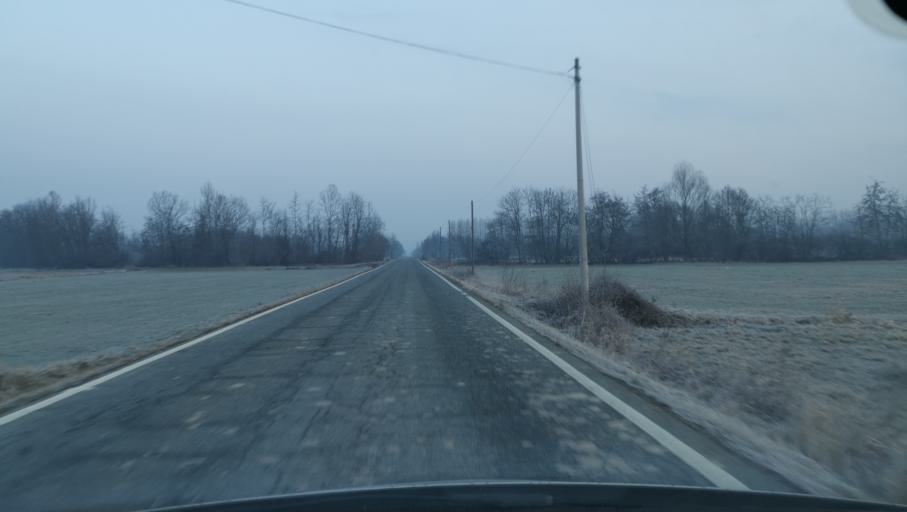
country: IT
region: Piedmont
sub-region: Provincia di Torino
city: Foglizzo
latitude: 45.2814
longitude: 7.8118
